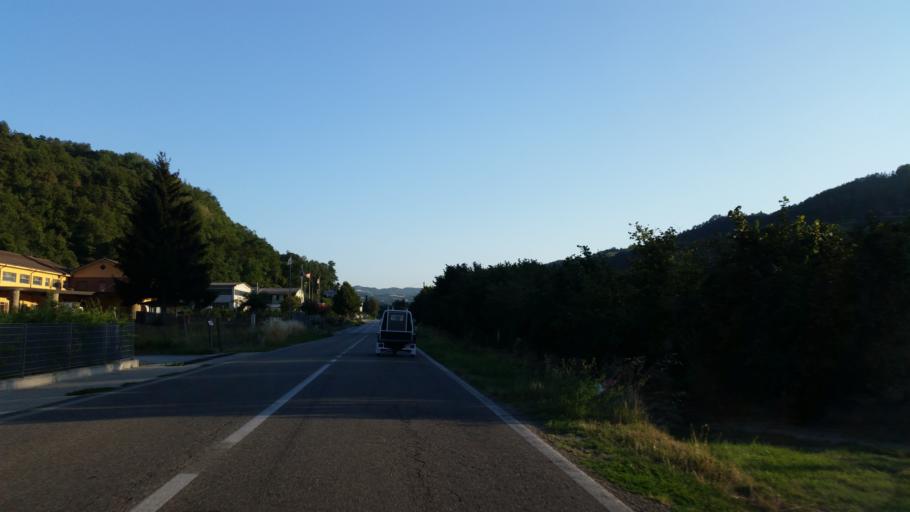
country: IT
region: Piedmont
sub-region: Provincia di Cuneo
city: Camo
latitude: 44.6862
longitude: 8.2036
